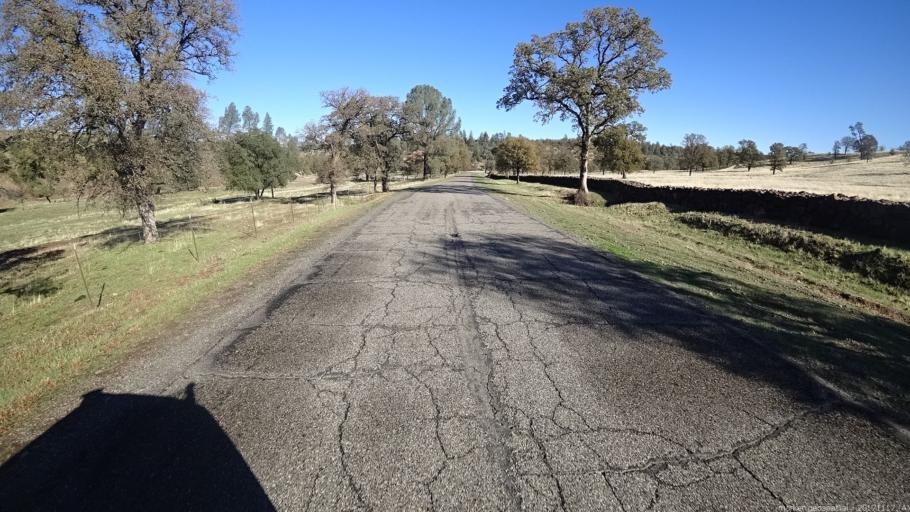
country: US
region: California
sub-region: Shasta County
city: Cottonwood
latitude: 40.4392
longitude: -122.1631
